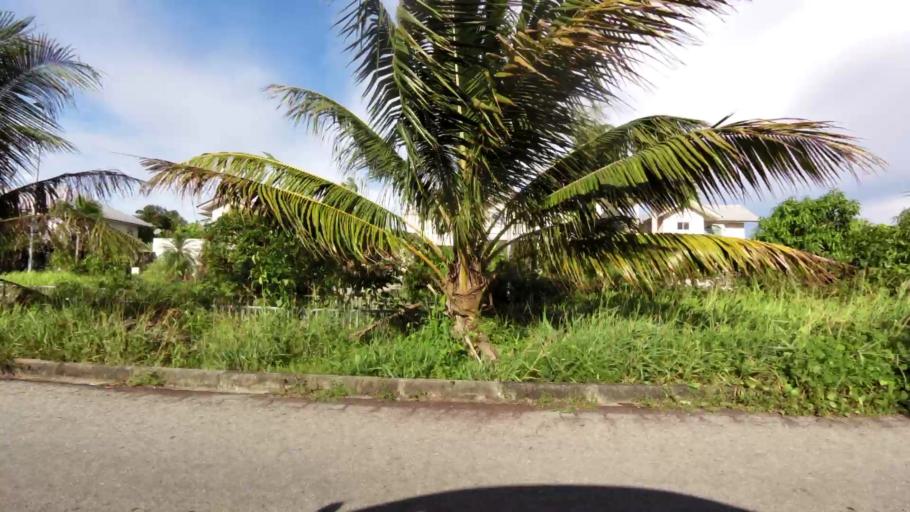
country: BN
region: Brunei and Muara
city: Bandar Seri Begawan
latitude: 4.9832
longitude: 114.9609
